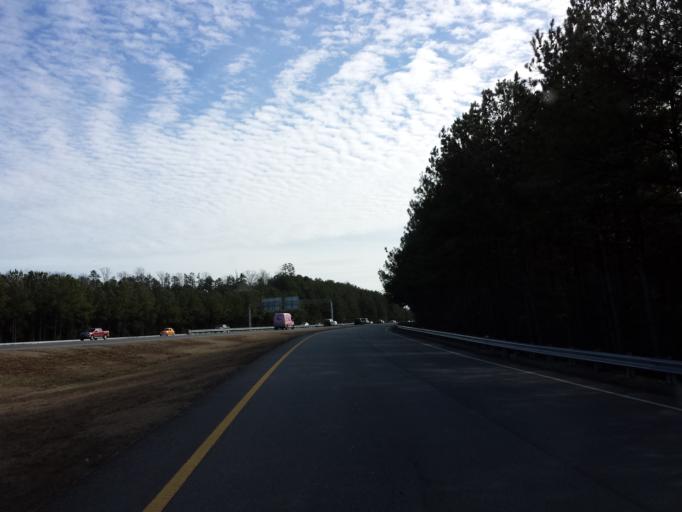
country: US
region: Georgia
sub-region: Cobb County
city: Kennesaw
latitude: 34.0107
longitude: -84.5598
